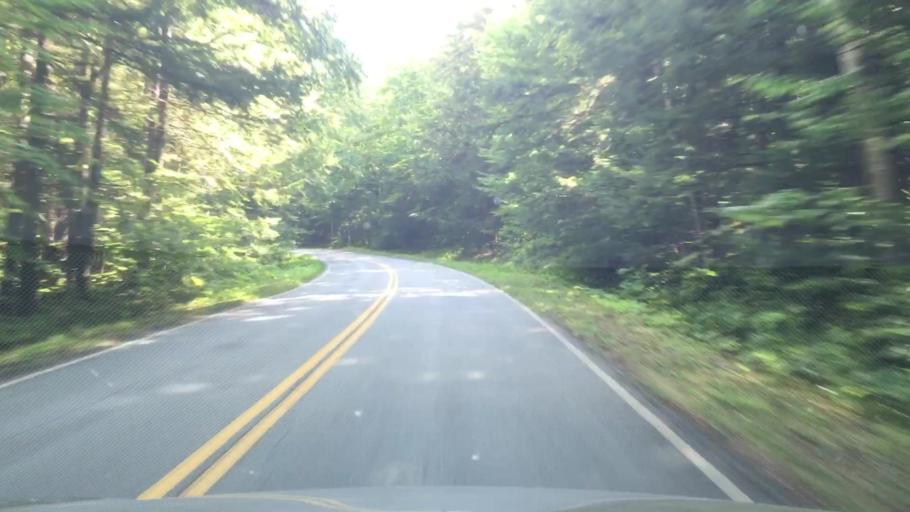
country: US
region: New Hampshire
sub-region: Carroll County
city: North Conway
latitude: 44.0647
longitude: -71.2824
